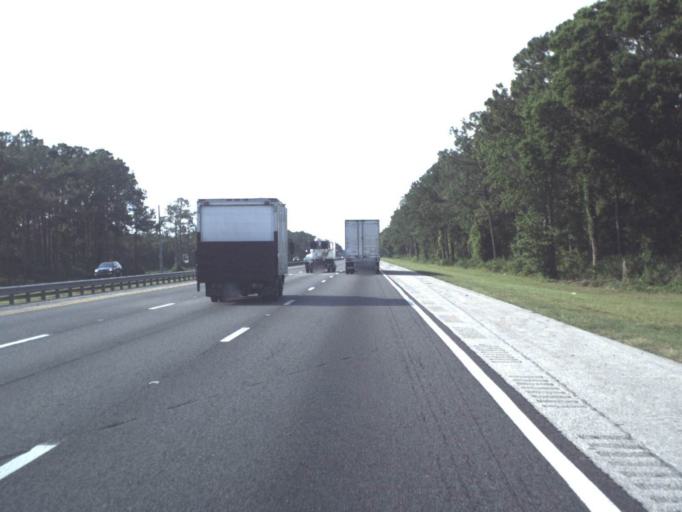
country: US
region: Florida
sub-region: Saint Johns County
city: Saint Augustine Shores
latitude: 29.7820
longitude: -81.3600
